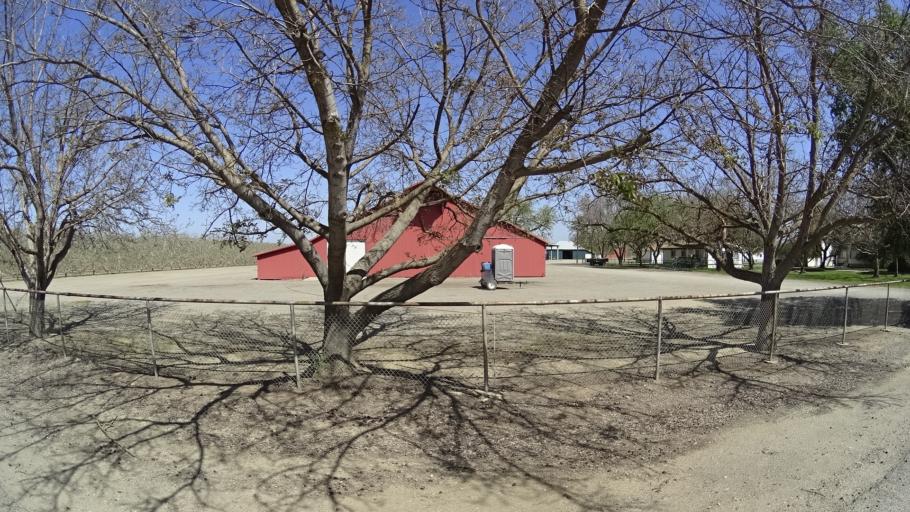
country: US
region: California
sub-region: Glenn County
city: Willows
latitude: 39.4990
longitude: -122.0276
